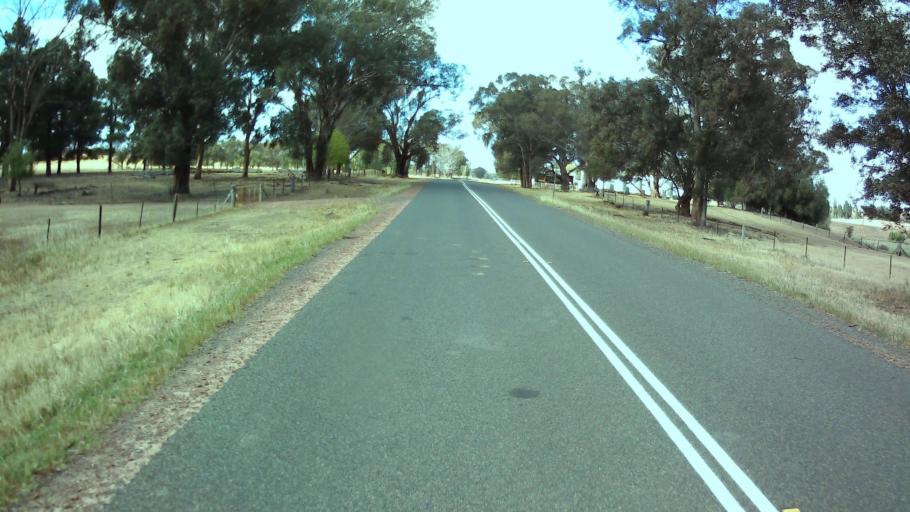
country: AU
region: New South Wales
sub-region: Weddin
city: Grenfell
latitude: -33.9531
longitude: 148.4396
